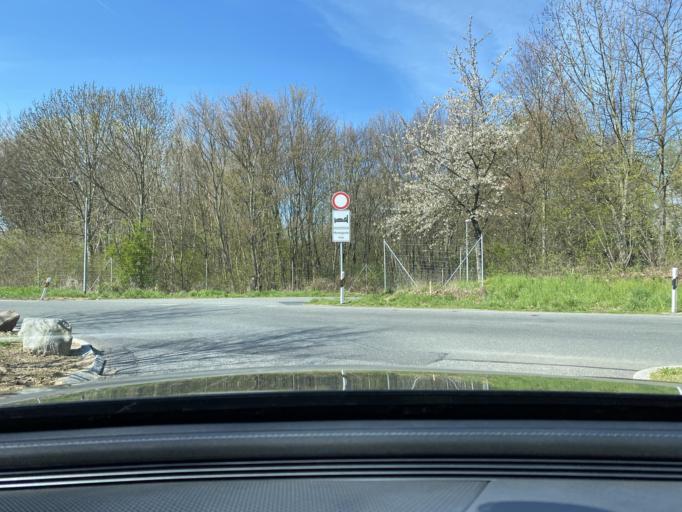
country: DE
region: Saxony
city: Wilsdruff
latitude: 51.0627
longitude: 13.5686
